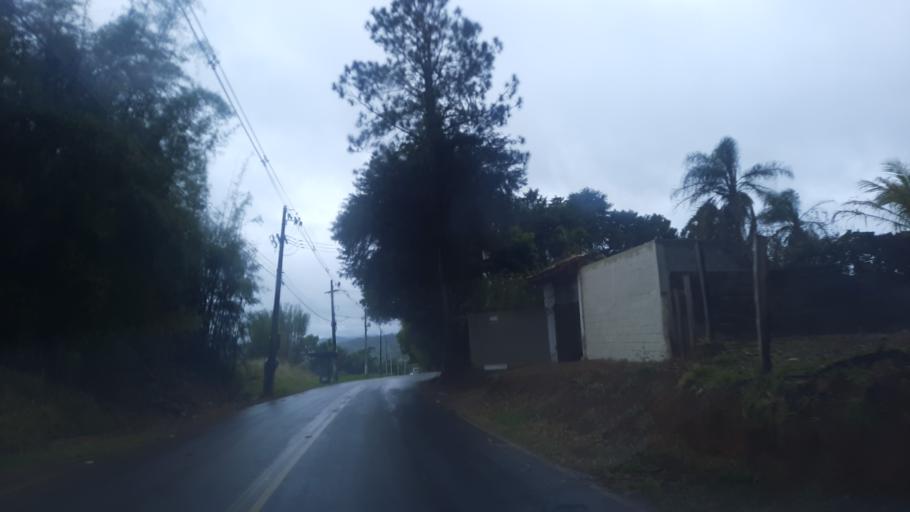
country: BR
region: Sao Paulo
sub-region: Atibaia
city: Atibaia
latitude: -23.0715
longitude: -46.5166
